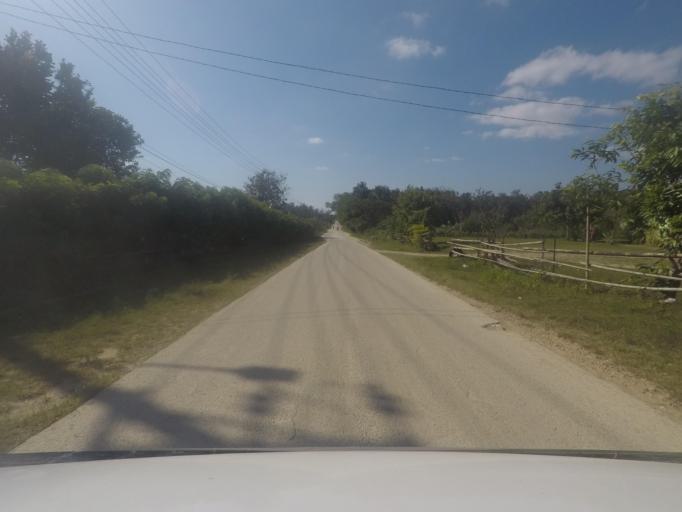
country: TL
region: Lautem
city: Lospalos
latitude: -8.4772
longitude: 126.9926
